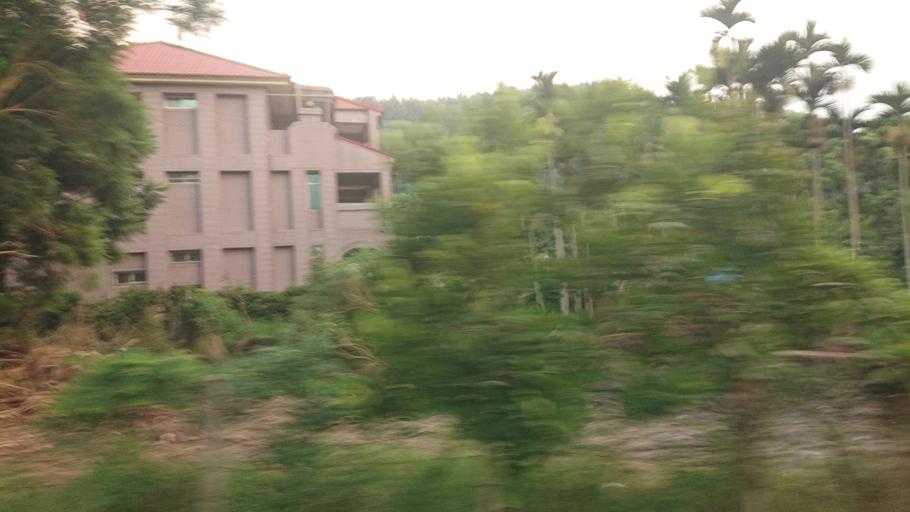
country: TW
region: Taiwan
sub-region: Nantou
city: Puli
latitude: 23.9731
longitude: 120.9938
